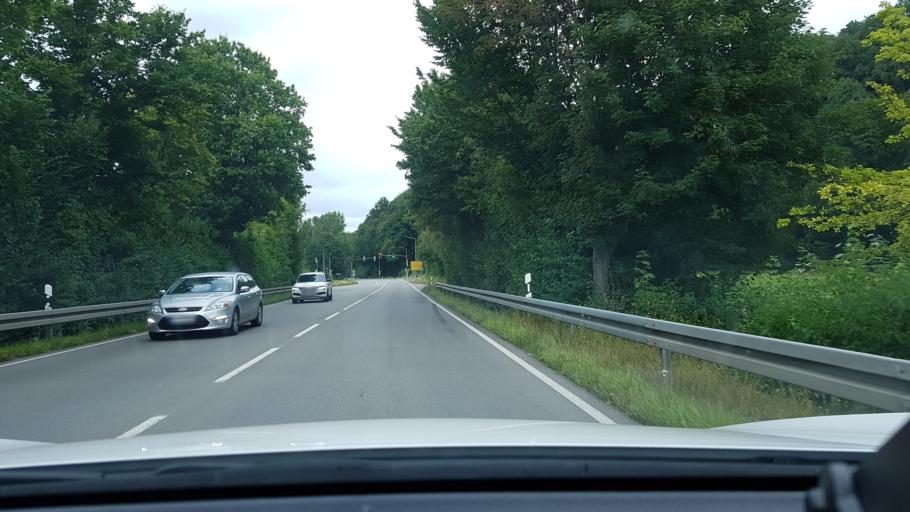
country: DE
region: Baden-Wuerttemberg
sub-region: Tuebingen Region
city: Warthausen
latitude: 48.1296
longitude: 9.8061
